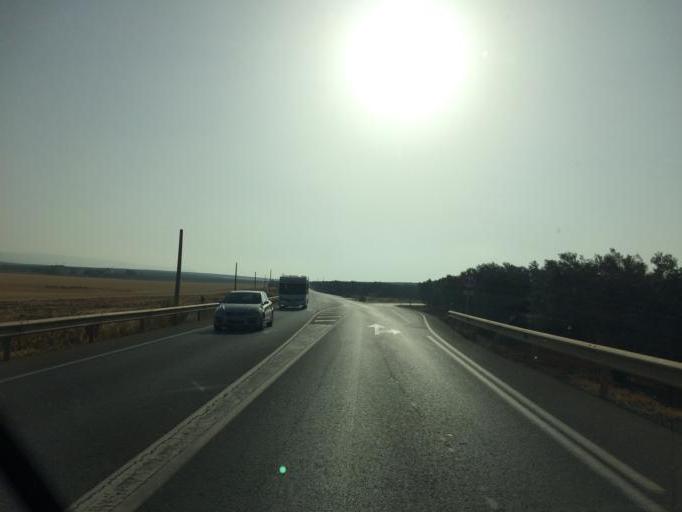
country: ES
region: Andalusia
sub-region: Provincia de Malaga
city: Humilladero
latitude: 37.0526
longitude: -4.7557
